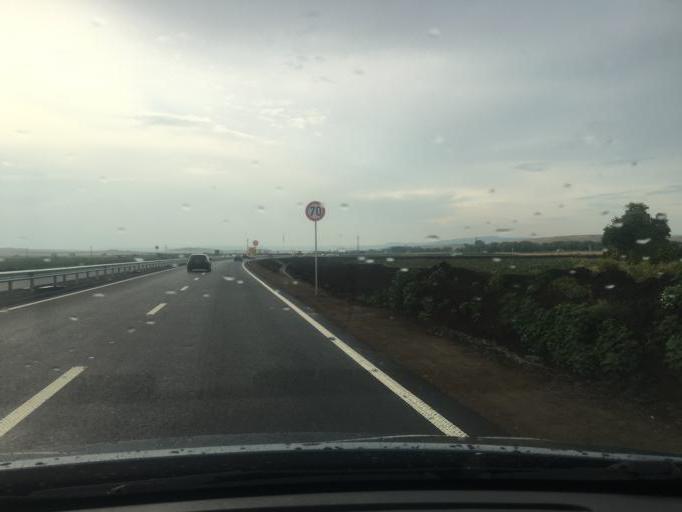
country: BG
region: Burgas
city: Aheloy
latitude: 42.6427
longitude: 27.6380
